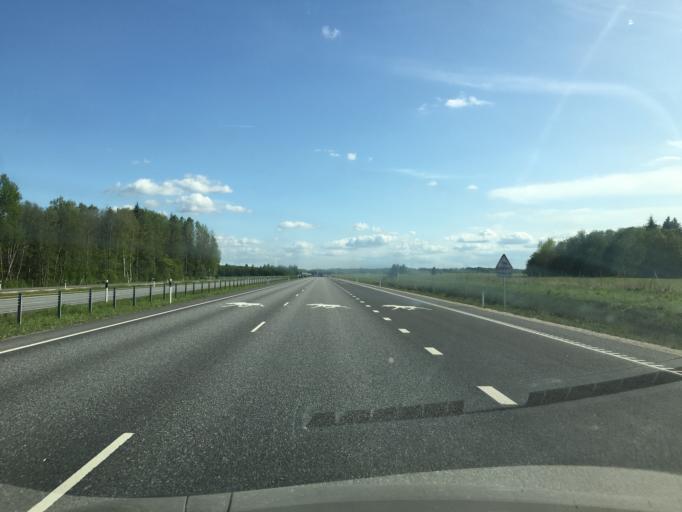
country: EE
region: Harju
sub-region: Rae vald
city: Vaida
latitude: 59.2130
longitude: 25.0370
